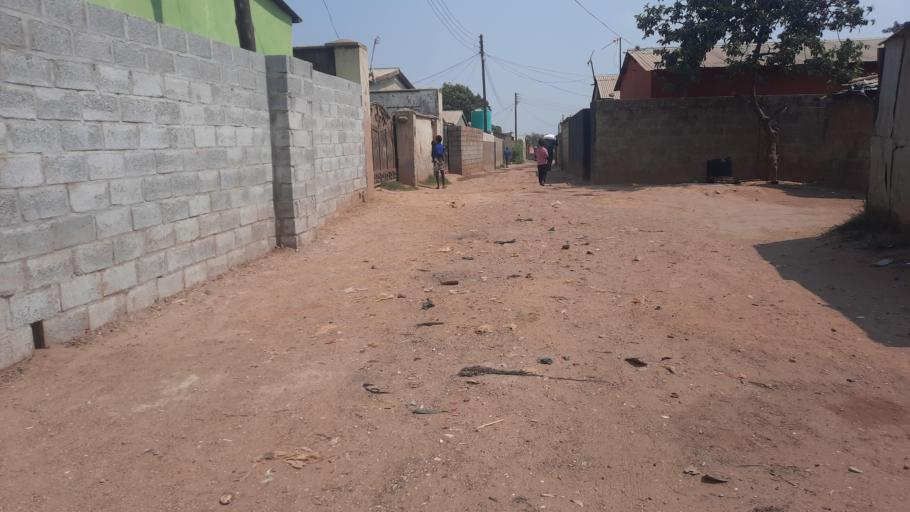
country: ZM
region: Lusaka
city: Lusaka
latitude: -15.4032
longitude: 28.3768
